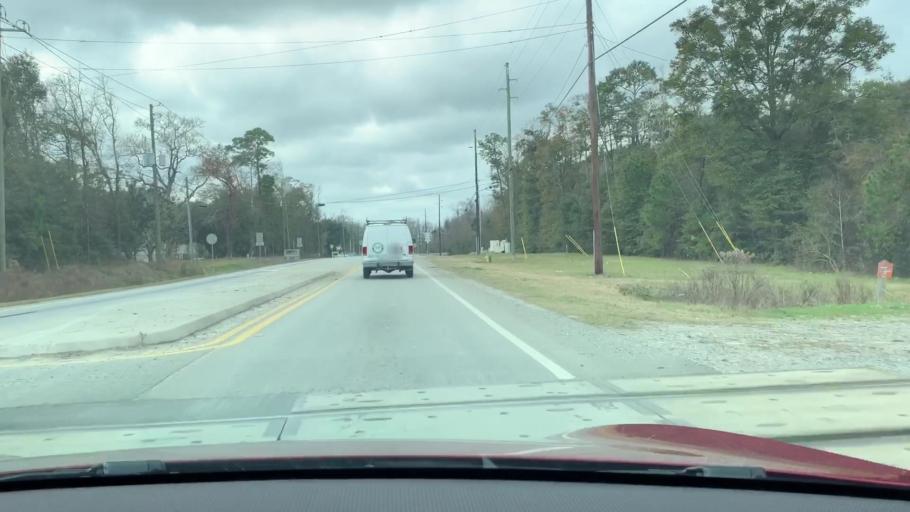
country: US
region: Georgia
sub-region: Chatham County
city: Port Wentworth
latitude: 32.1435
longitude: -81.1883
